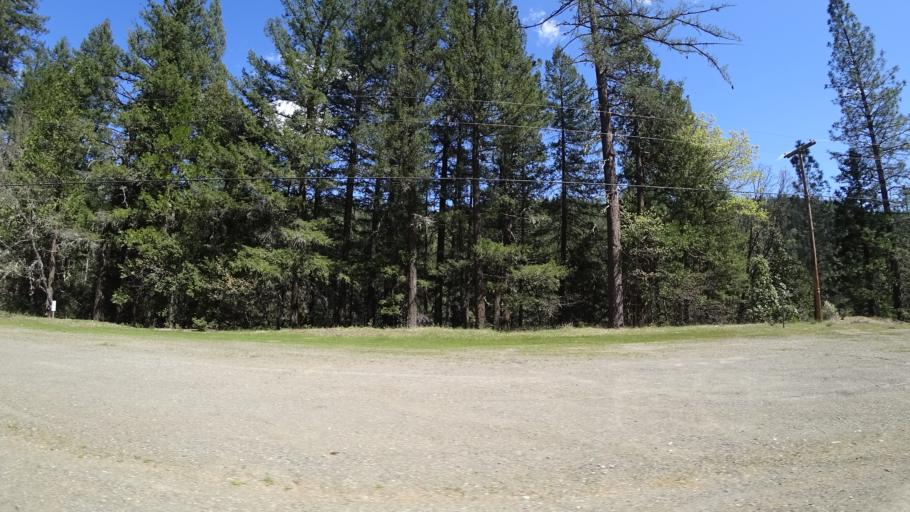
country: US
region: California
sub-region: Trinity County
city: Weaverville
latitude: 40.7511
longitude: -122.8870
